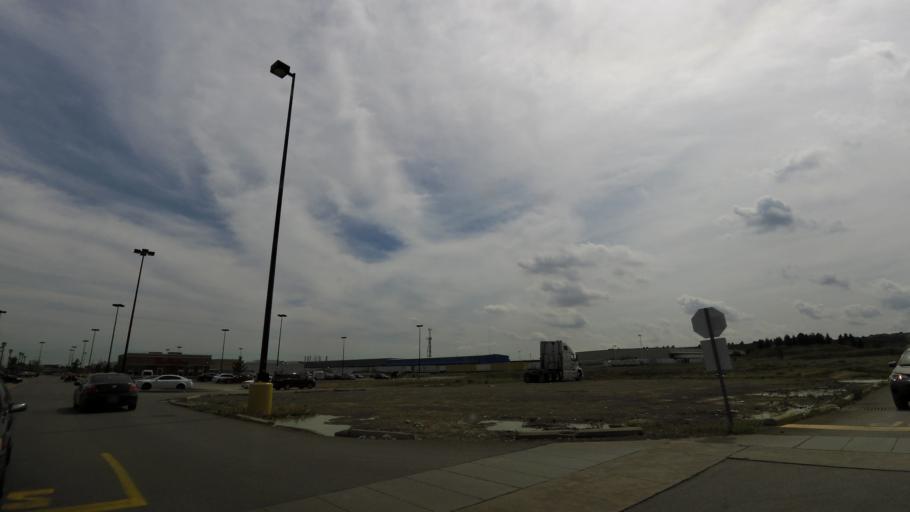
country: CA
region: Ontario
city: Brampton
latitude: 43.7615
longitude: -79.7213
